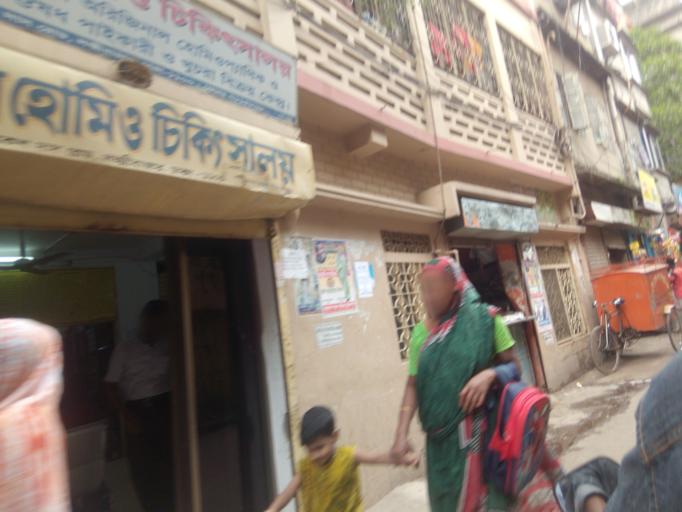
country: BD
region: Dhaka
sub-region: Dhaka
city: Dhaka
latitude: 23.7081
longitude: 90.4178
